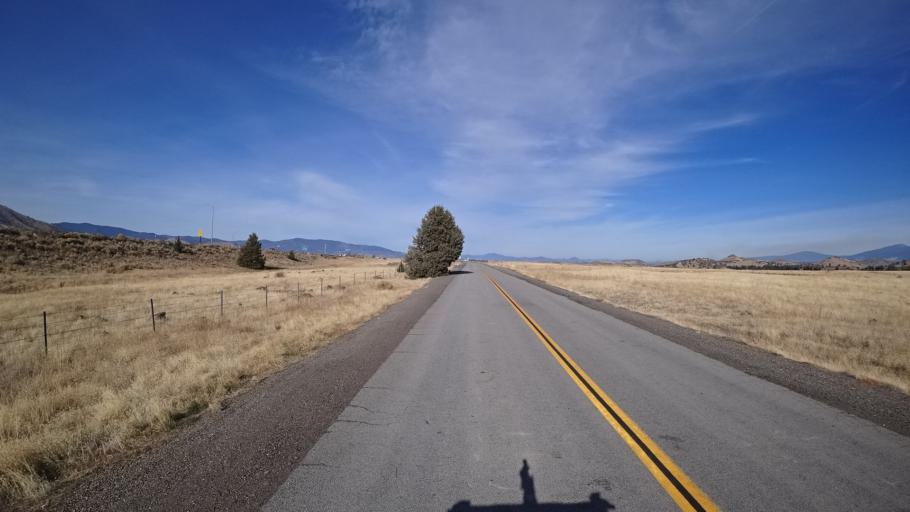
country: US
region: California
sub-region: Siskiyou County
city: Weed
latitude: 41.4721
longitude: -122.4510
